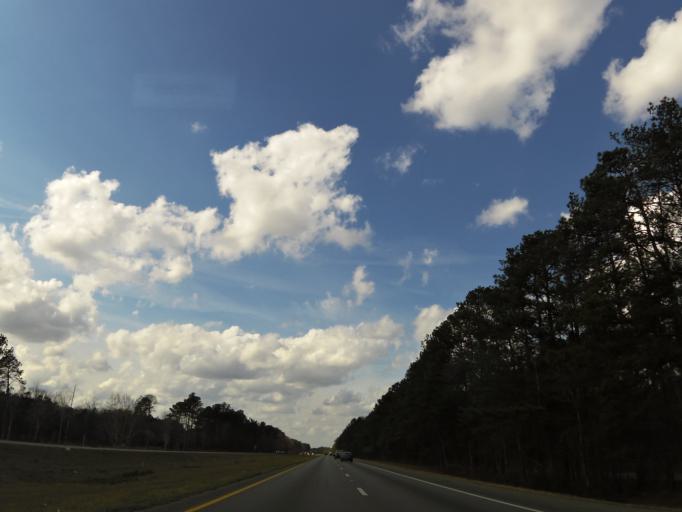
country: US
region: South Carolina
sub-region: Dorchester County
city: Summerville
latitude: 33.0749
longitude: -80.1964
